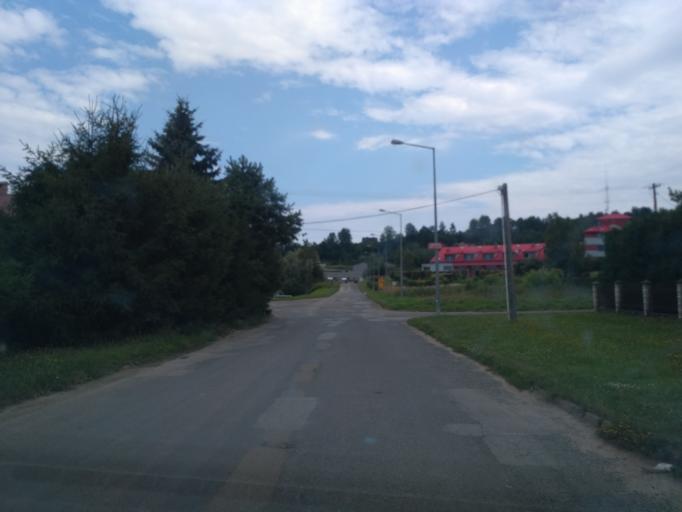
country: PL
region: Subcarpathian Voivodeship
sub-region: Powiat sanocki
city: Sanok
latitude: 49.5704
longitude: 22.1651
